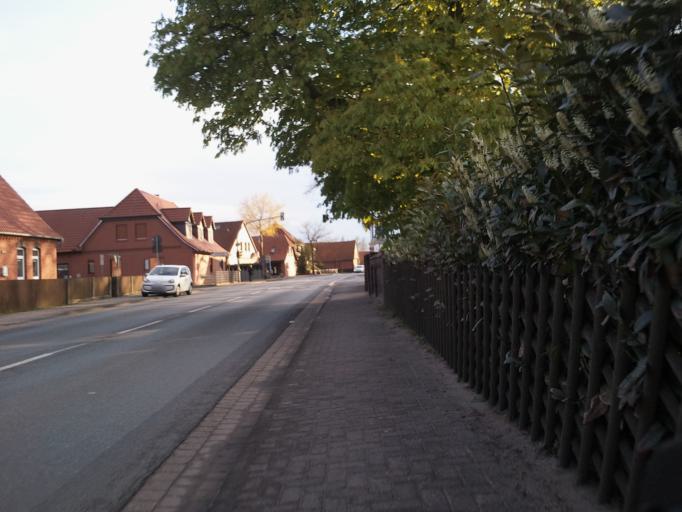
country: DE
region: Lower Saxony
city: Nienburg
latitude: 52.6627
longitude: 9.2441
